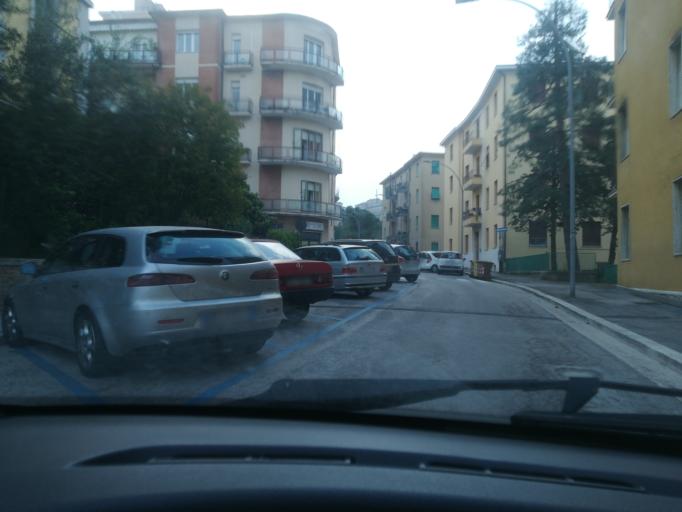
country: IT
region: The Marches
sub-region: Provincia di Macerata
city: Macerata
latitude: 43.2985
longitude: 13.4447
